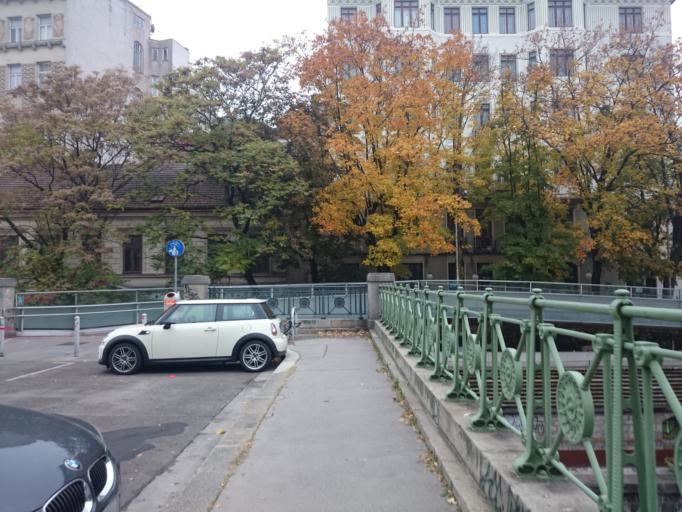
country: AT
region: Vienna
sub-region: Wien Stadt
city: Vienna
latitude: 48.1957
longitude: 16.3548
